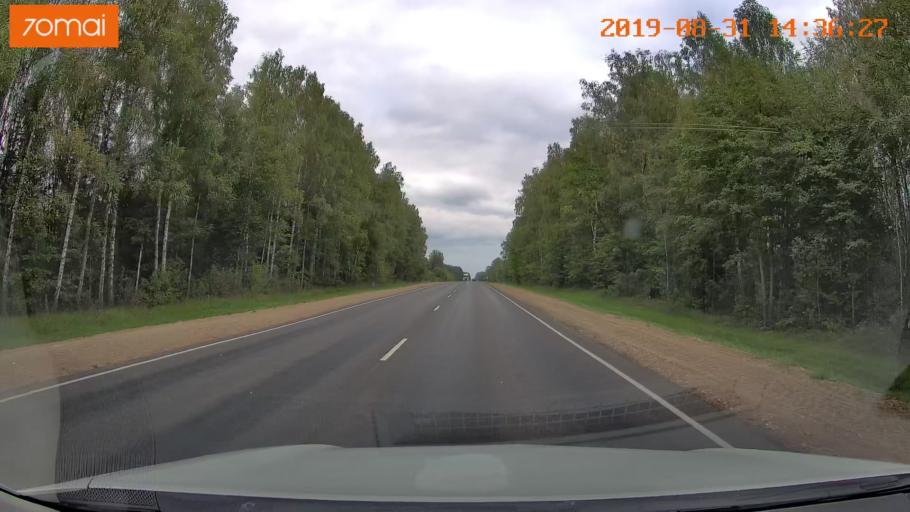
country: RU
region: Smolensk
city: Yekimovichi
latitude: 54.1701
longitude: 33.4802
